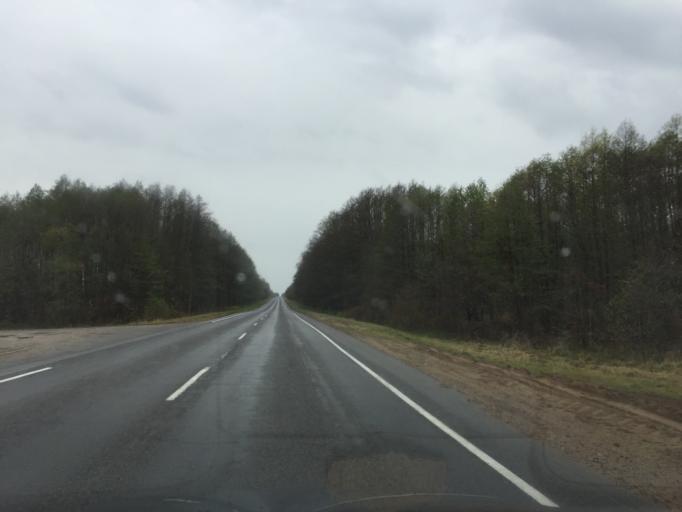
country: BY
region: Mogilev
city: Slawharad
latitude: 53.3867
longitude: 30.8941
